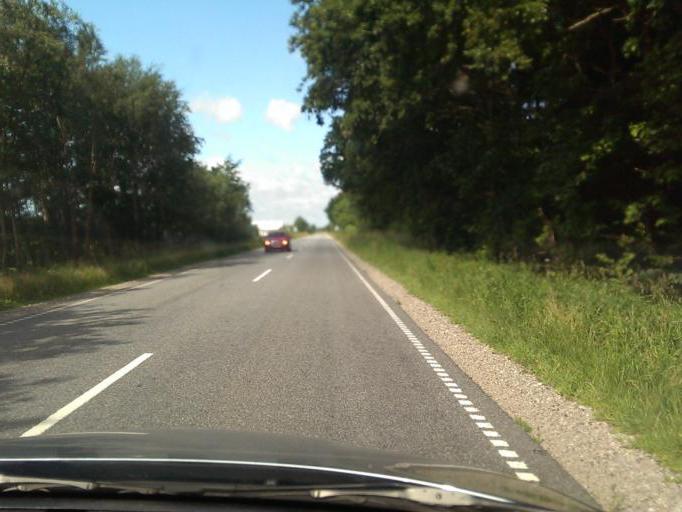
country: DK
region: North Denmark
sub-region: Jammerbugt Kommune
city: Abybro
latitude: 57.2053
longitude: 9.7868
